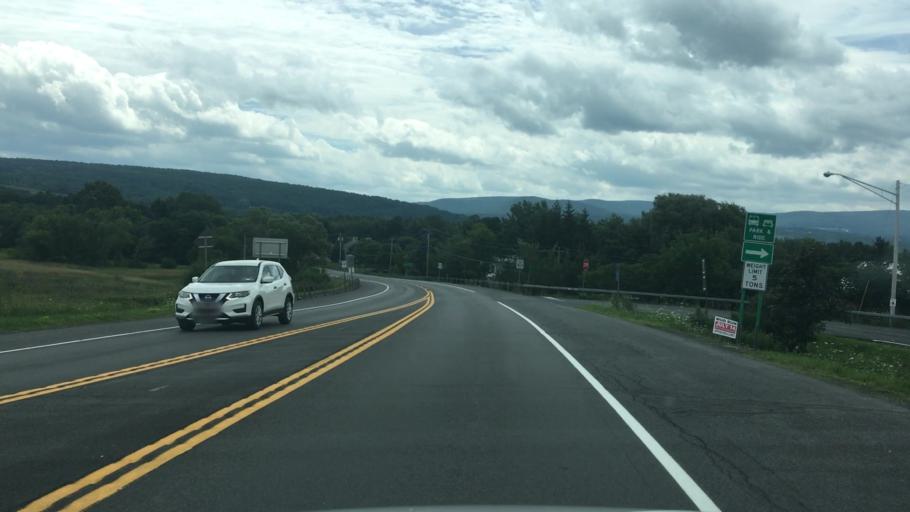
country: US
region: New York
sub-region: Schoharie County
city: Schoharie
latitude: 42.7057
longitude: -74.3131
